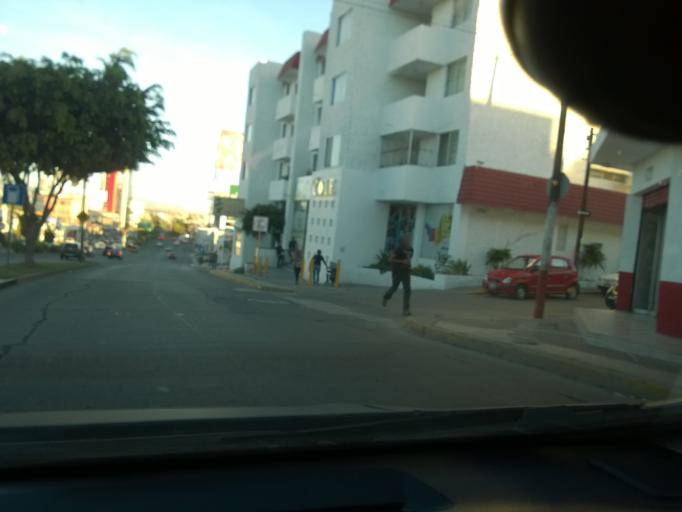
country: MX
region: Guanajuato
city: Leon
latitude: 21.1436
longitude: -101.6936
